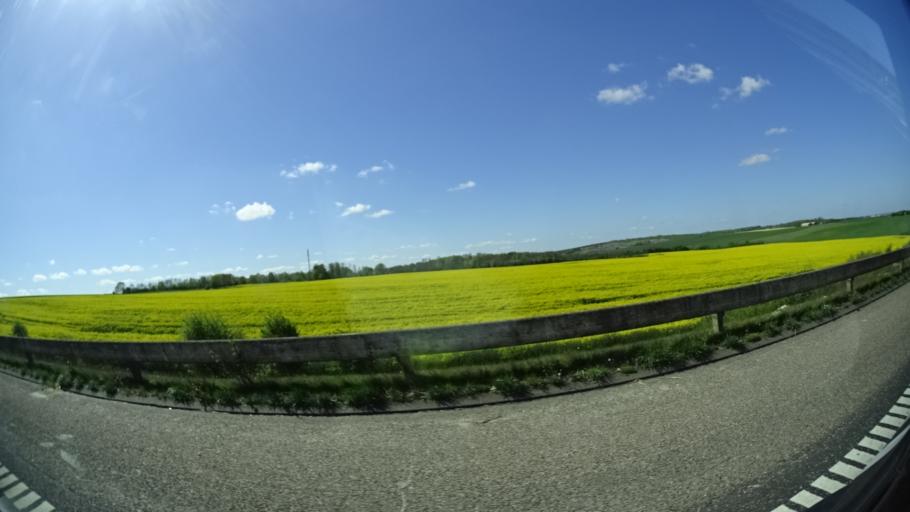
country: DK
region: Central Jutland
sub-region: Randers Kommune
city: Assentoft
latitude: 56.3747
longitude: 10.1176
